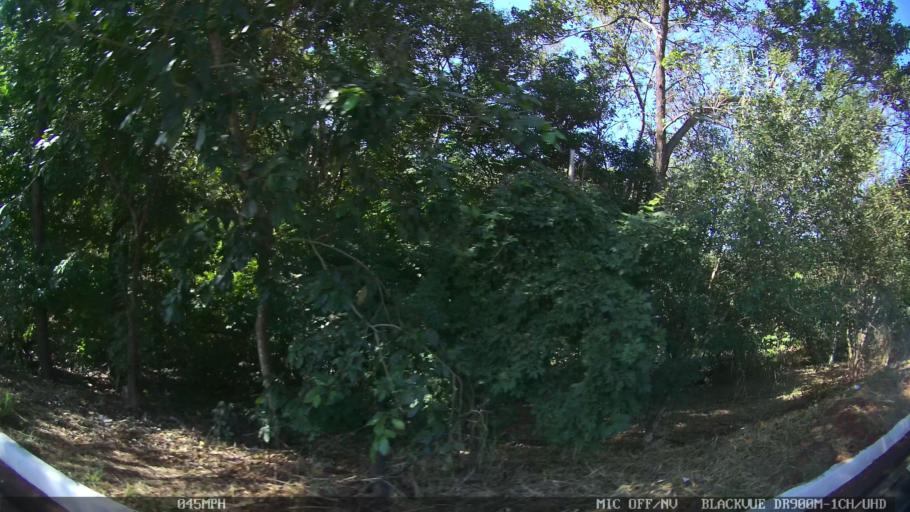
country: BR
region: Sao Paulo
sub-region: Ribeirao Preto
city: Ribeirao Preto
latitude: -21.2318
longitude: -47.7662
